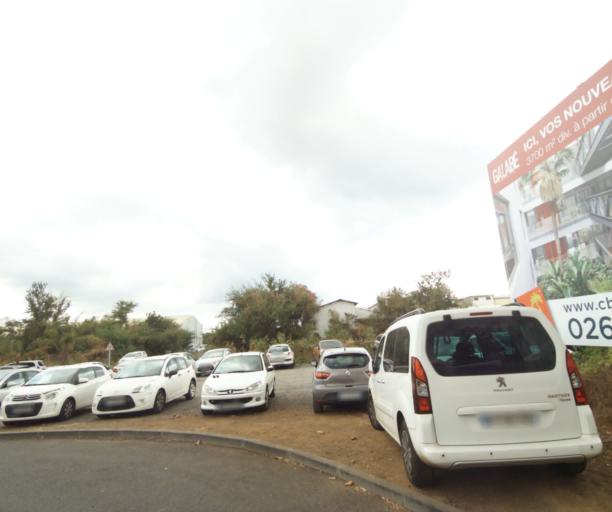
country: RE
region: Reunion
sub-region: Reunion
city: Saint-Paul
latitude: -20.9871
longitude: 55.2968
